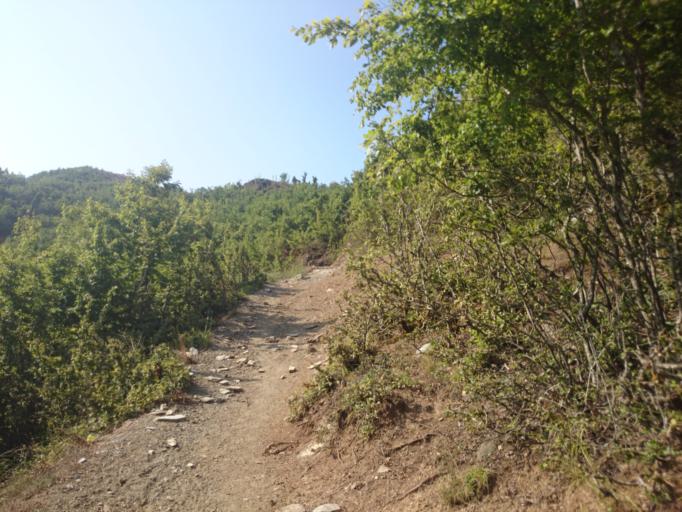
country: AL
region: Diber
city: Peshkopi
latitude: 41.6445
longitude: 20.3969
